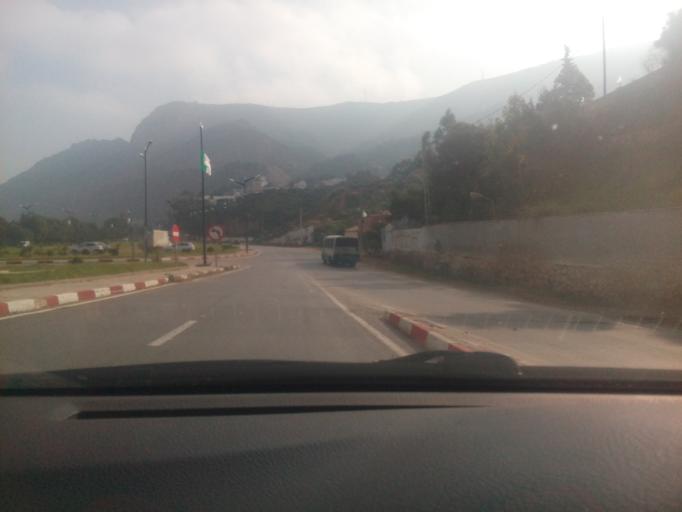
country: DZ
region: Oran
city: Mers el Kebir
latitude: 35.7142
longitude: -0.6895
